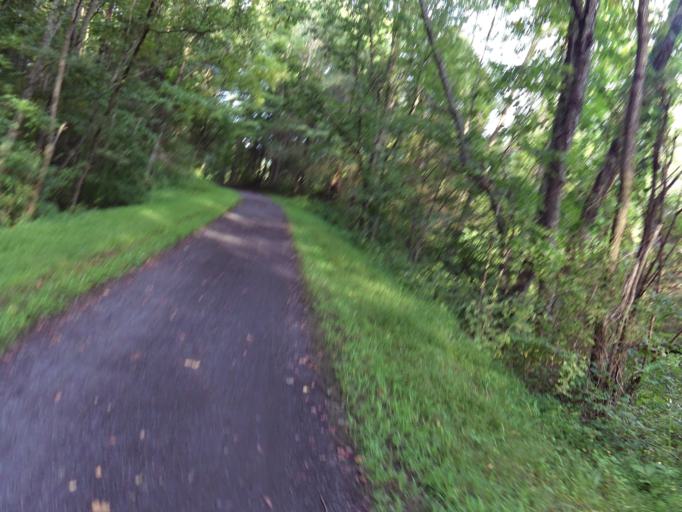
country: US
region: Virginia
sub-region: Washington County
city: Abingdon
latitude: 36.6800
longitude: -81.9424
